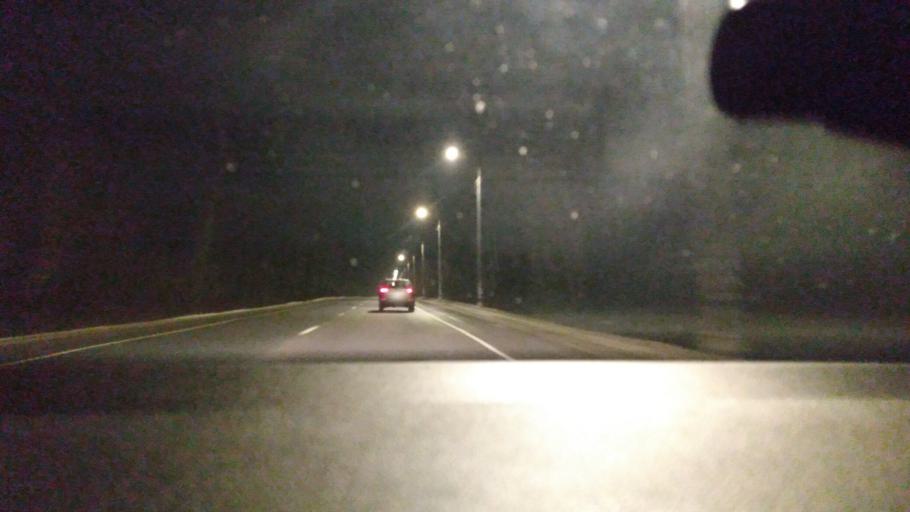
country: RU
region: Moskovskaya
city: Il'inskiy Pogost
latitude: 55.4632
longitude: 38.9779
